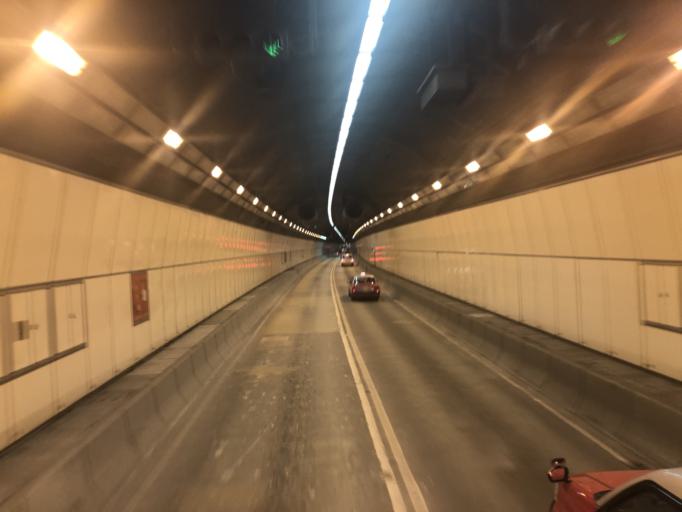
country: HK
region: Kowloon City
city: Kowloon
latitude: 22.3176
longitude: 114.2427
